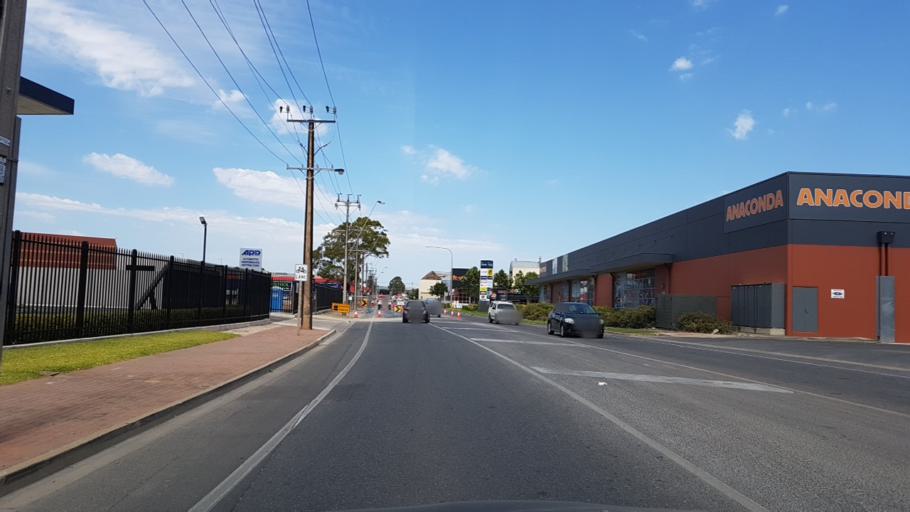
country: AU
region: South Australia
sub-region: Unley
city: Forestville
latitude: -34.9332
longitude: 138.5766
